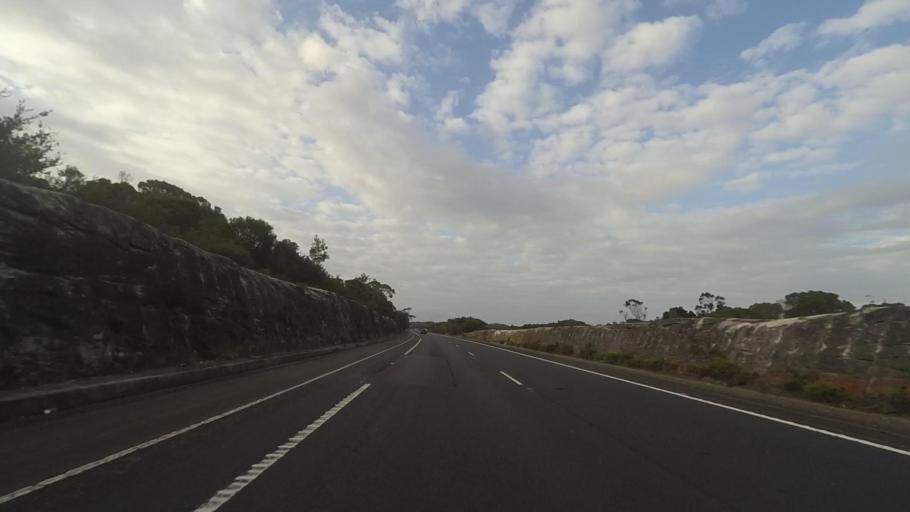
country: AU
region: New South Wales
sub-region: Wollongong
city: Bulli
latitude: -34.2790
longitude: 150.9281
